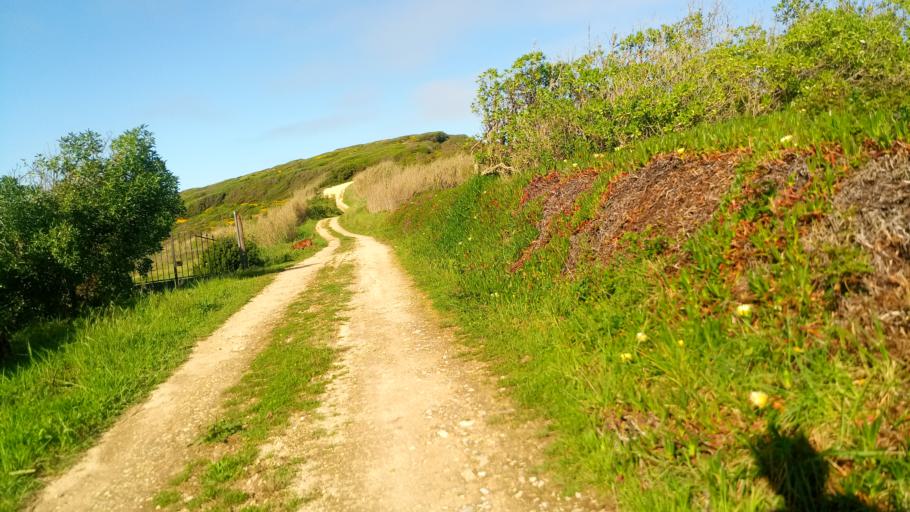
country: PT
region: Leiria
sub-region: Caldas da Rainha
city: Caldas da Rainha
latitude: 39.4922
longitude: -9.1749
